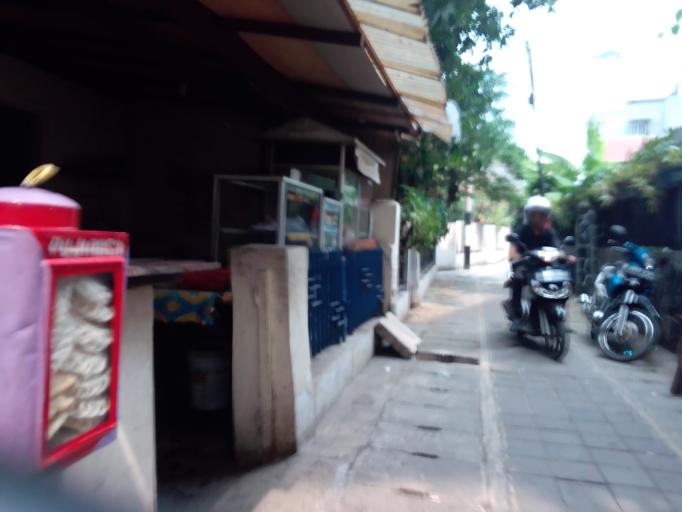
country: ID
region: Jakarta Raya
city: Jakarta
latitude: -6.1999
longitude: 106.8238
